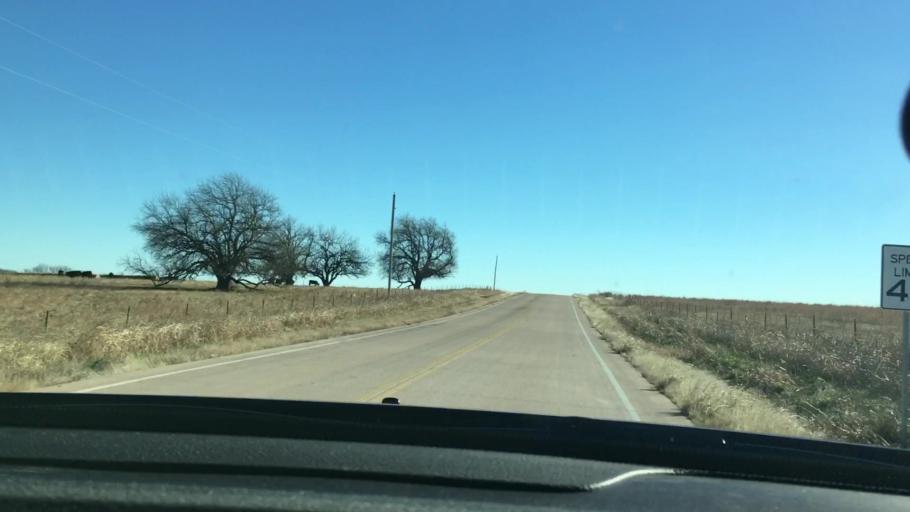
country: US
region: Oklahoma
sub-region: Marshall County
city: Madill
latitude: 34.1144
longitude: -96.7232
